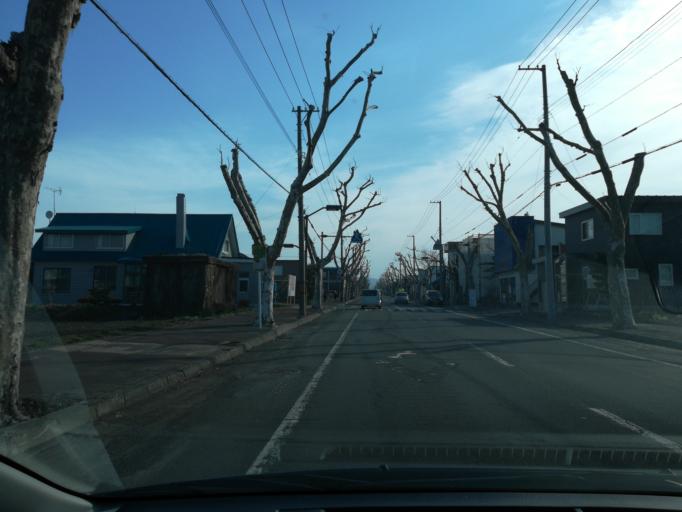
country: JP
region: Hokkaido
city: Iwamizawa
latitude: 43.2055
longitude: 141.7531
